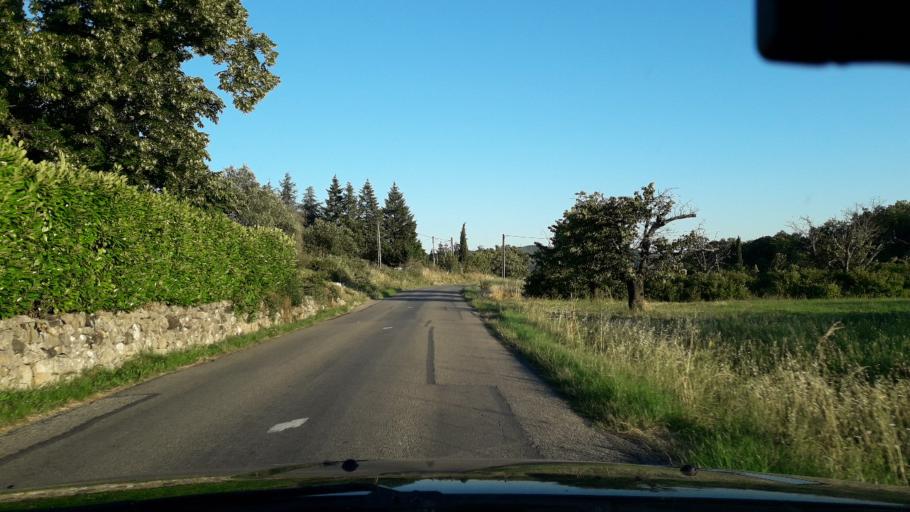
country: FR
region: Rhone-Alpes
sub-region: Departement de l'Ardeche
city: Lavilledieu
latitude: 44.5899
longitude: 4.4603
